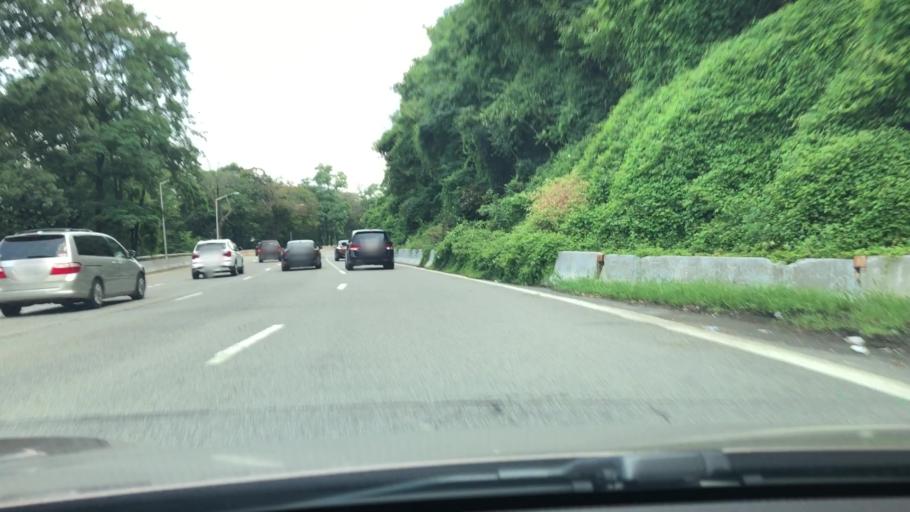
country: US
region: New York
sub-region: New York County
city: Inwood
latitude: 40.8539
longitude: -73.9403
